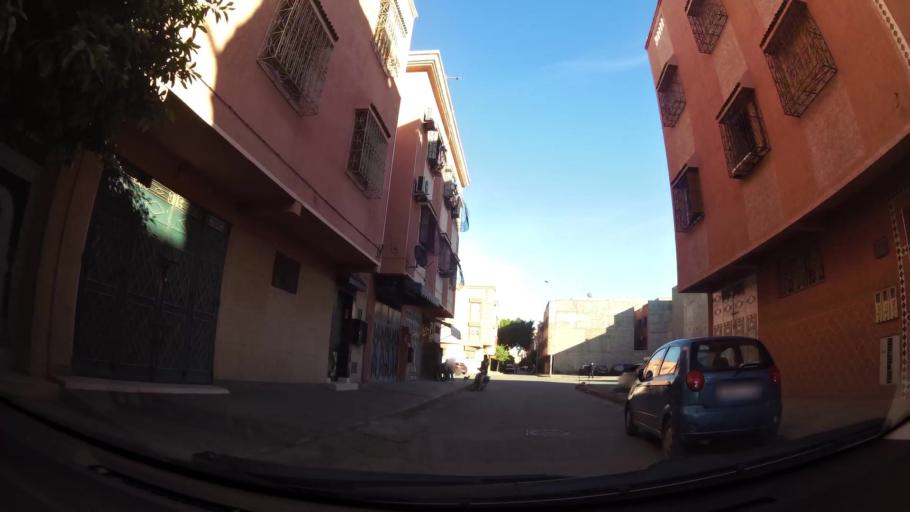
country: MA
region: Marrakech-Tensift-Al Haouz
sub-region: Marrakech
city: Marrakesh
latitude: 31.6180
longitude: -8.0655
